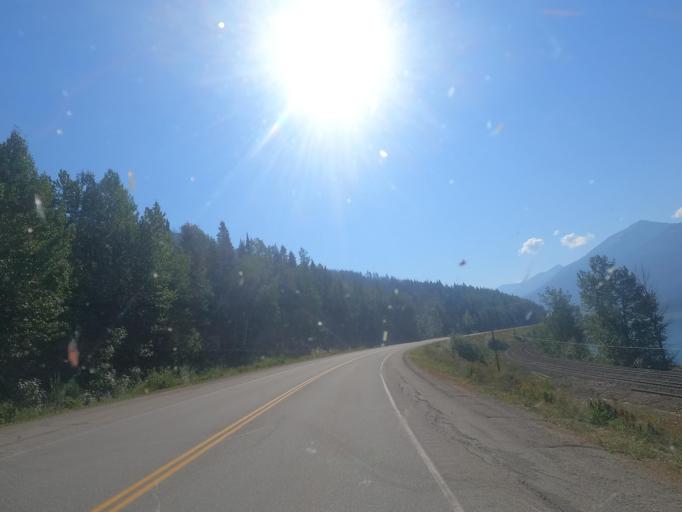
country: CA
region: Alberta
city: Jasper Park Lodge
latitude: 52.9516
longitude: -118.8664
